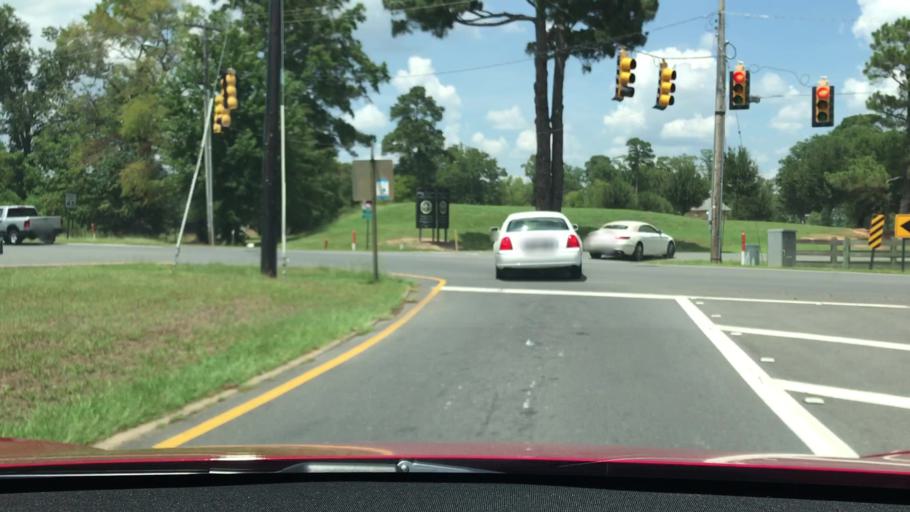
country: US
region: Louisiana
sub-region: Bossier Parish
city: Bossier City
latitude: 32.3834
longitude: -93.7138
